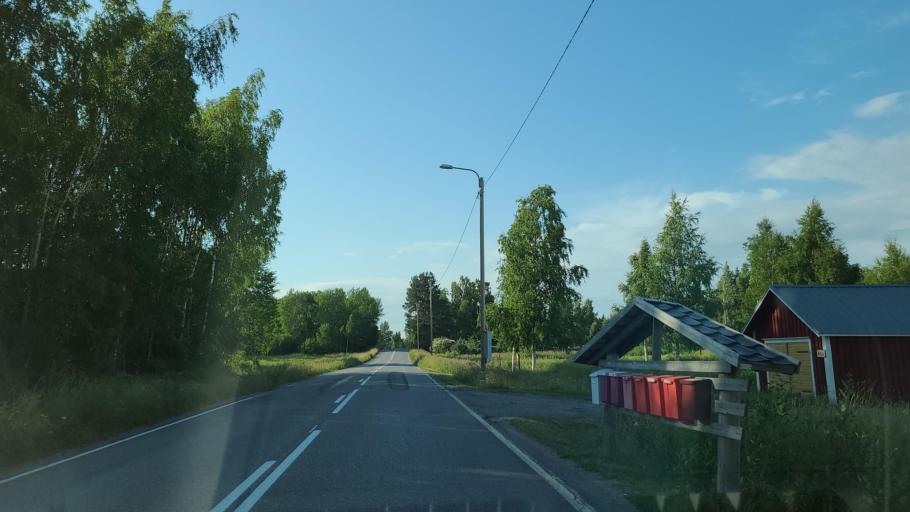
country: FI
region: Ostrobothnia
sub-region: Vaasa
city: Replot
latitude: 63.3340
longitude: 21.3348
